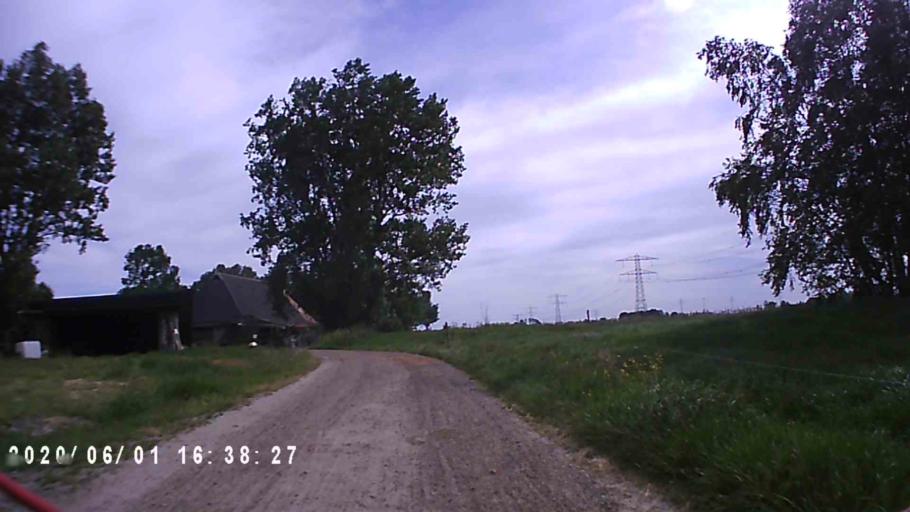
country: NL
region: Friesland
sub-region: Gemeente Leeuwarden
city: Camminghaburen
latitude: 53.1880
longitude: 5.8769
